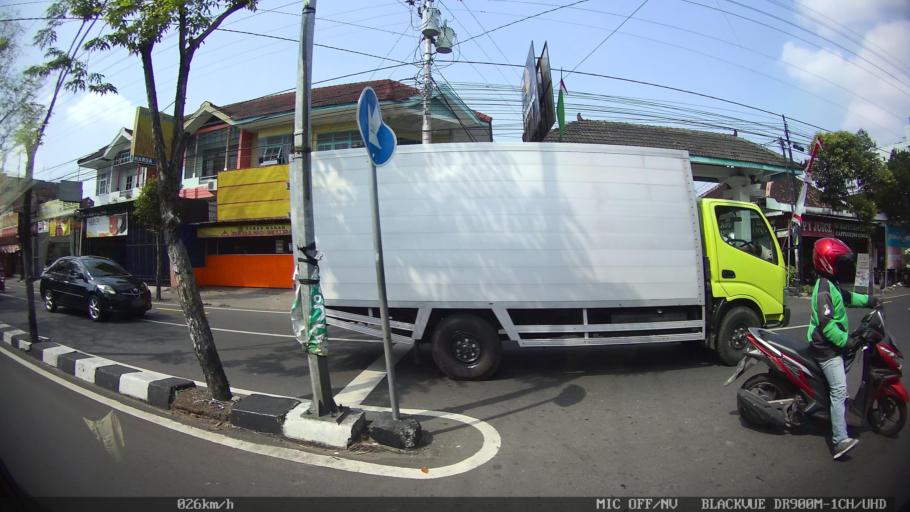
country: ID
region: Daerah Istimewa Yogyakarta
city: Yogyakarta
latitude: -7.8167
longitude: 110.3814
